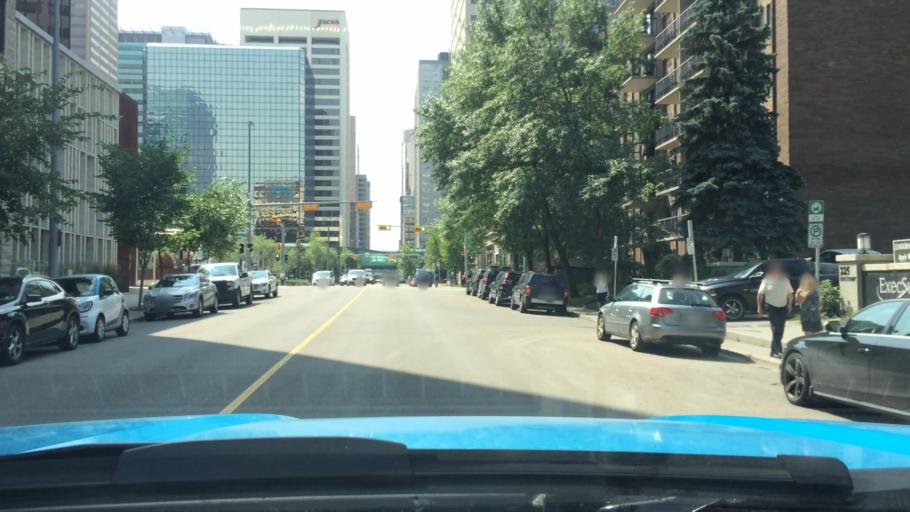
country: CA
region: Alberta
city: Calgary
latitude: 51.0515
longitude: -114.0761
